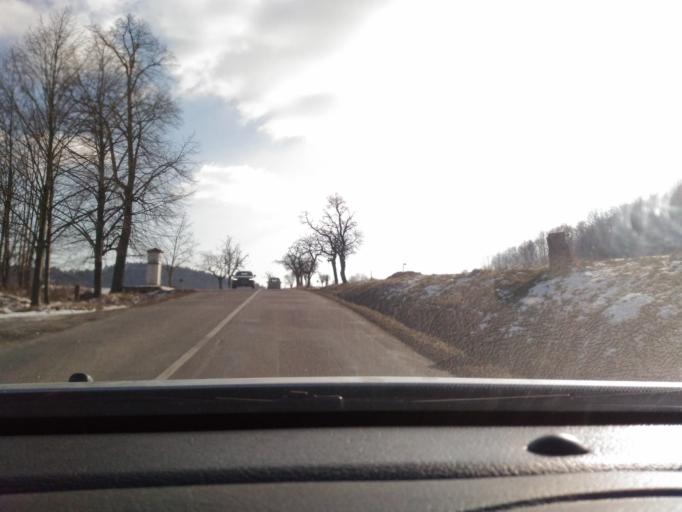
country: CZ
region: South Moravian
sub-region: Okres Brno-Venkov
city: Nedvedice
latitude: 49.4143
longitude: 16.3517
